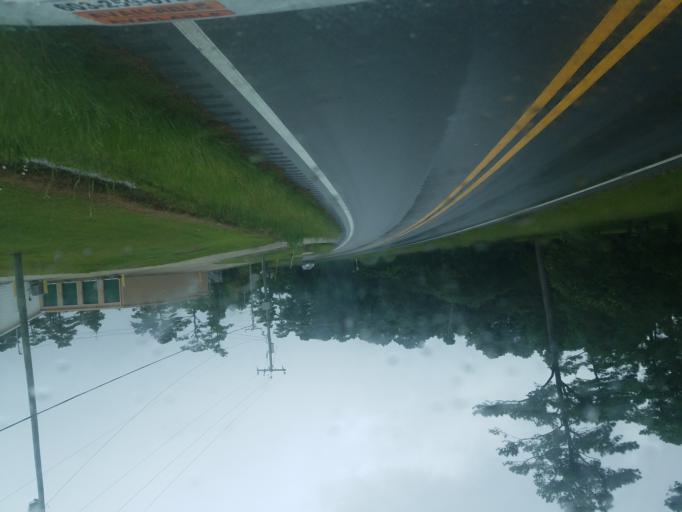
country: US
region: North Carolina
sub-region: Dare County
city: Manteo
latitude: 35.8793
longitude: -75.6596
